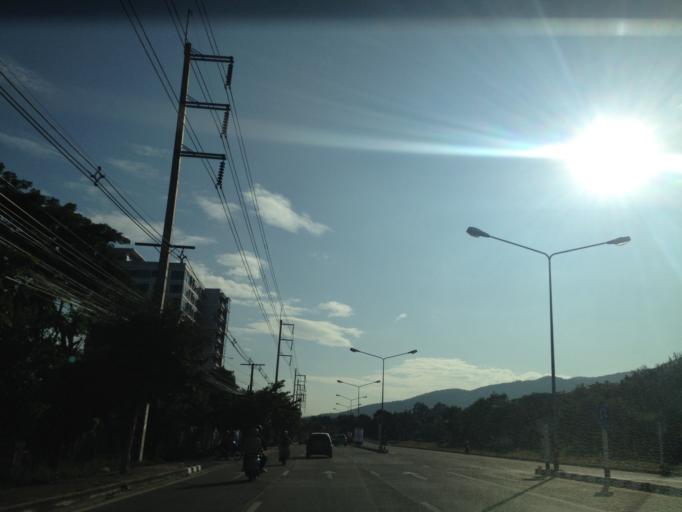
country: TH
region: Chiang Mai
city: Chiang Mai
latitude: 18.8205
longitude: 98.9647
